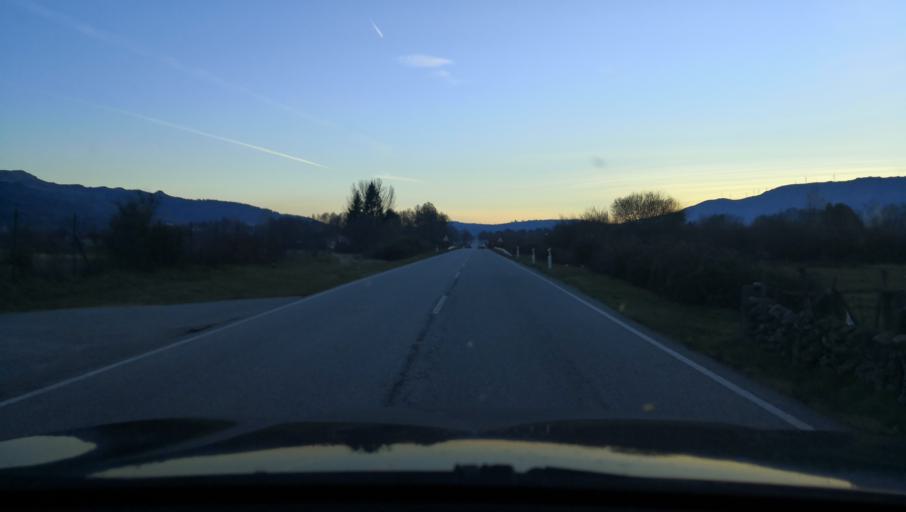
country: PT
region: Vila Real
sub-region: Vila Pouca de Aguiar
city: Vila Pouca de Aguiar
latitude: 41.4459
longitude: -7.6722
